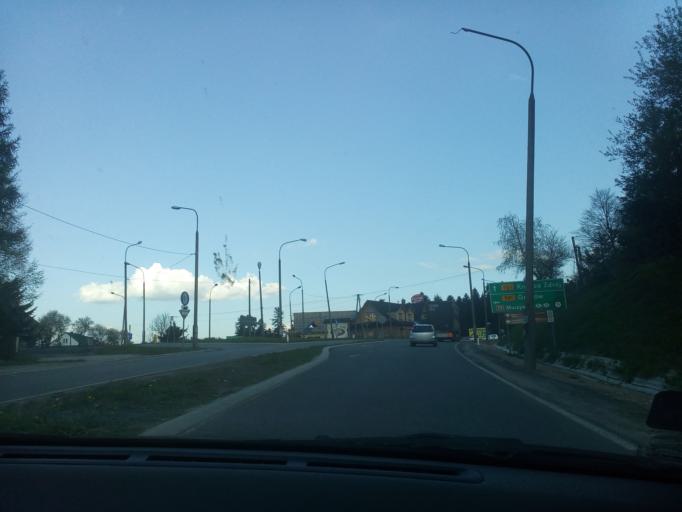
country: PL
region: Lesser Poland Voivodeship
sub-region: Powiat nowosadecki
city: Krynica-Zdroj
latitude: 49.4642
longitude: 20.9531
